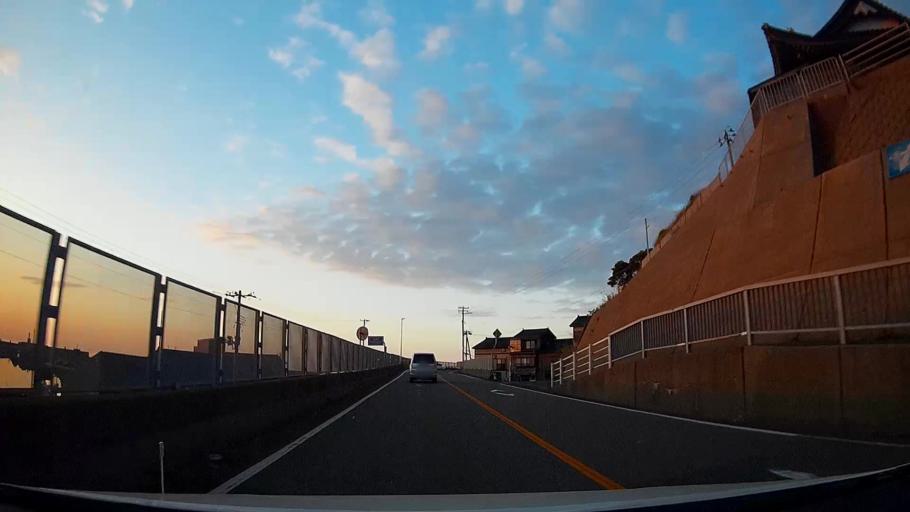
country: JP
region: Niigata
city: Joetsu
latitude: 37.1335
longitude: 138.0536
